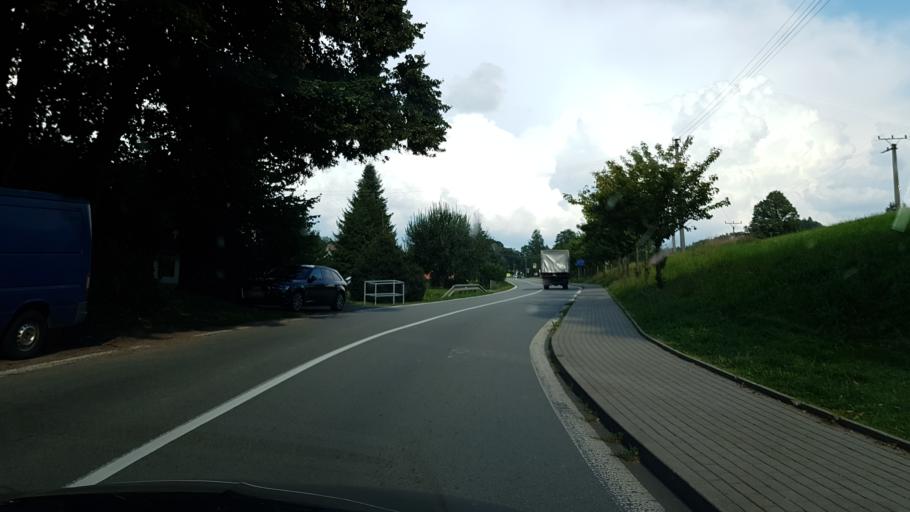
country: CZ
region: Pardubicky
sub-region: Okres Usti nad Orlici
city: Kunvald
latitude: 50.0946
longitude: 16.5632
